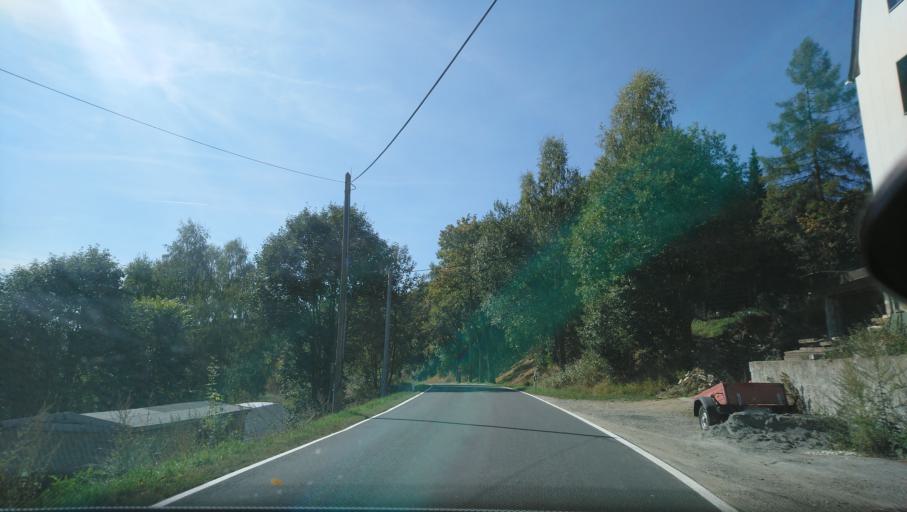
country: DE
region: Saxony
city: Barenstein
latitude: 50.5111
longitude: 13.0302
